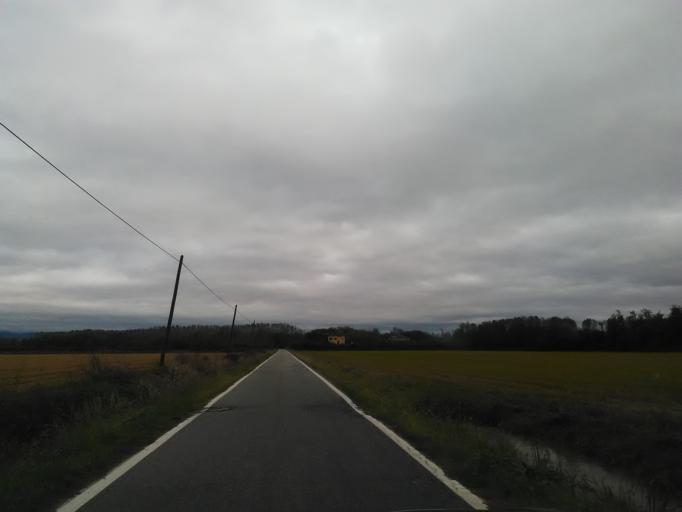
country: IT
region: Piedmont
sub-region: Provincia di Vercelli
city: Carisio
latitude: 45.3979
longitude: 8.2433
